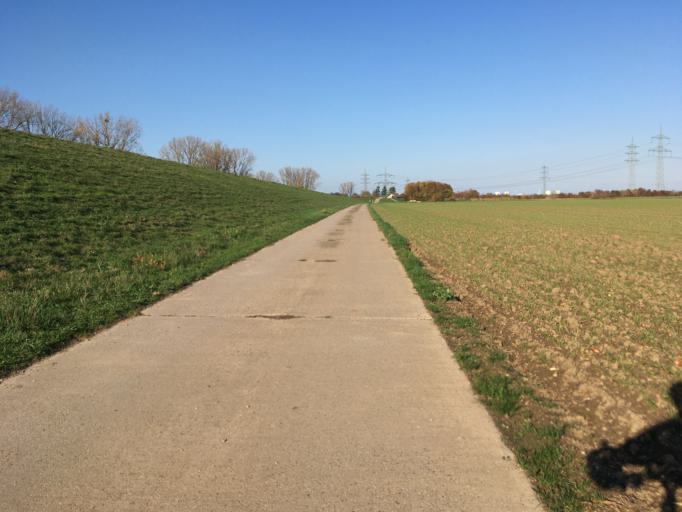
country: DE
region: Rheinland-Pfalz
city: Worms
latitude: 49.6575
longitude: 8.3883
